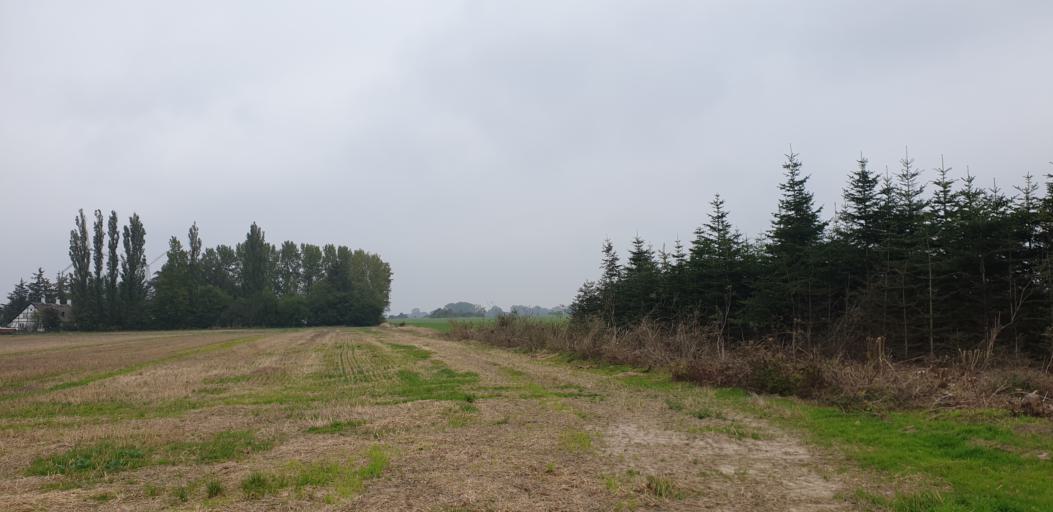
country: DK
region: Zealand
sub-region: Stevns Kommune
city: Harlev
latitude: 55.3344
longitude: 12.2000
